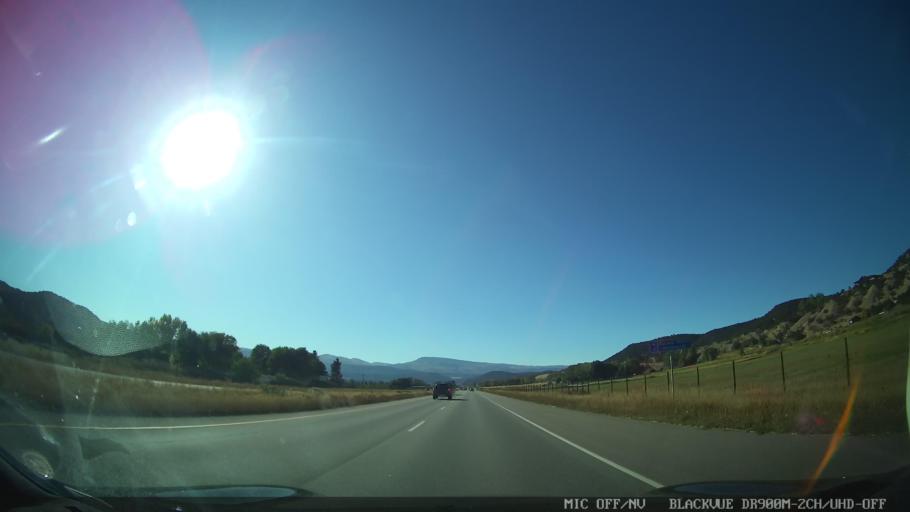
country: US
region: Colorado
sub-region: Eagle County
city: El Jebel
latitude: 39.4075
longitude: -107.1459
